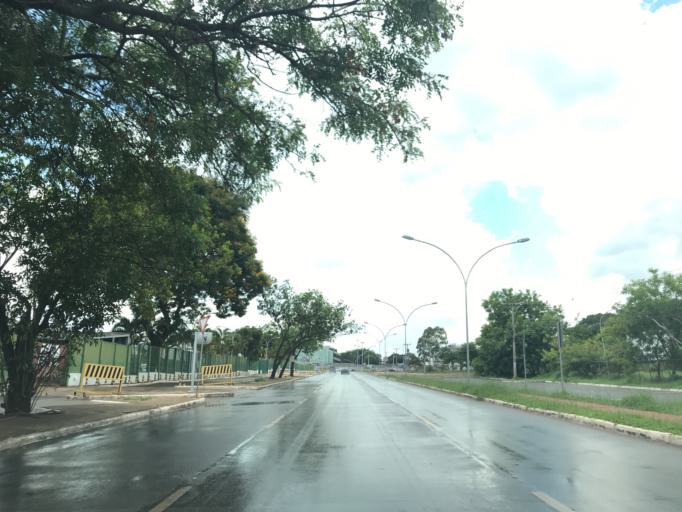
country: BR
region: Federal District
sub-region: Brasilia
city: Brasilia
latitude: -15.7671
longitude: -47.8945
